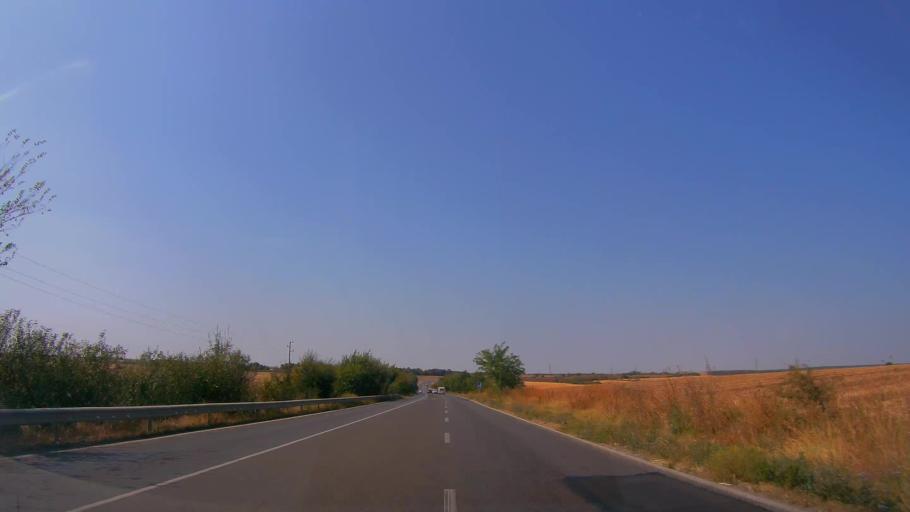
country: BG
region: Ruse
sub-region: Obshtina Vetovo
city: Senovo
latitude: 43.5660
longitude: 26.3319
